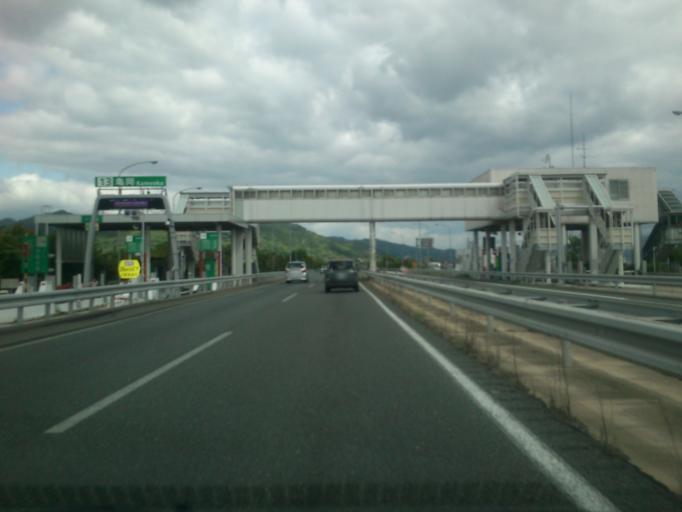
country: JP
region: Kyoto
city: Kameoka
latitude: 35.0145
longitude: 135.5566
